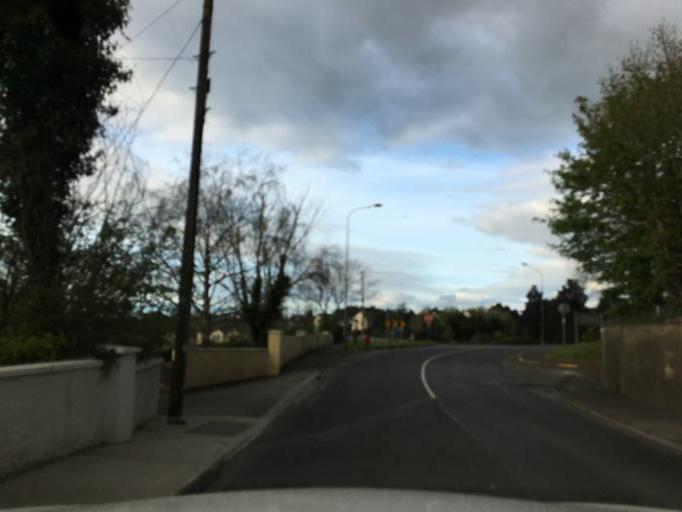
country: IE
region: Leinster
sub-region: Loch Garman
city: New Ross
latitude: 52.4024
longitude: -6.9374
